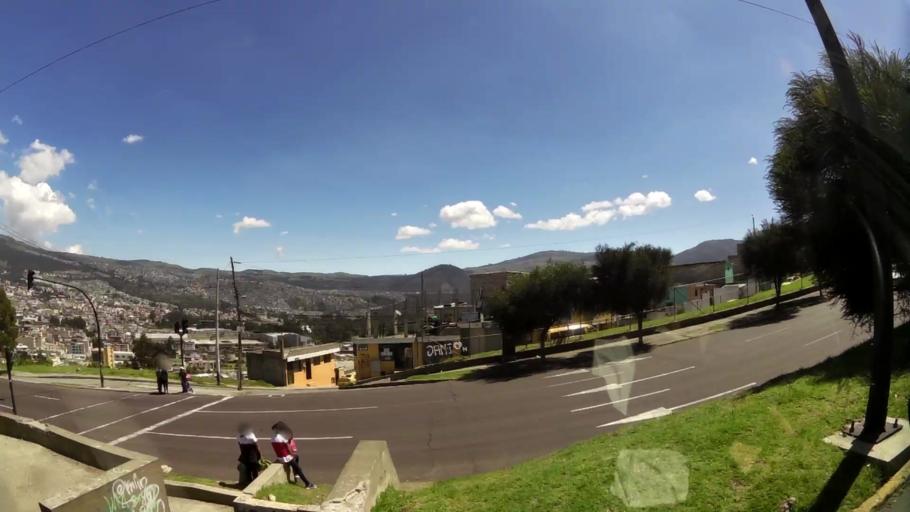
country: EC
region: Pichincha
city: Quito
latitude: -0.1063
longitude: -78.4847
